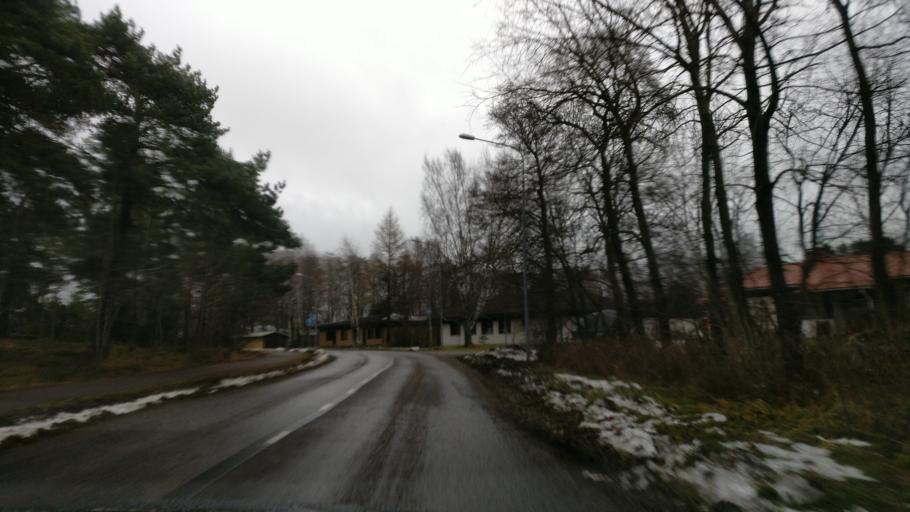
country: FI
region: Uusimaa
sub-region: Raaseporin
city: Hanko
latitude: 59.8329
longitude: 22.9365
